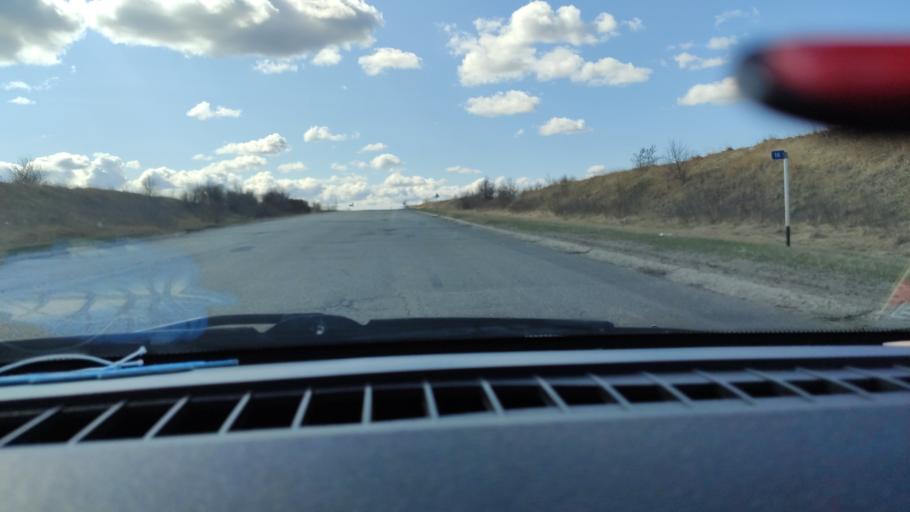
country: RU
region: Samara
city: Varlamovo
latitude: 53.0870
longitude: 48.3549
